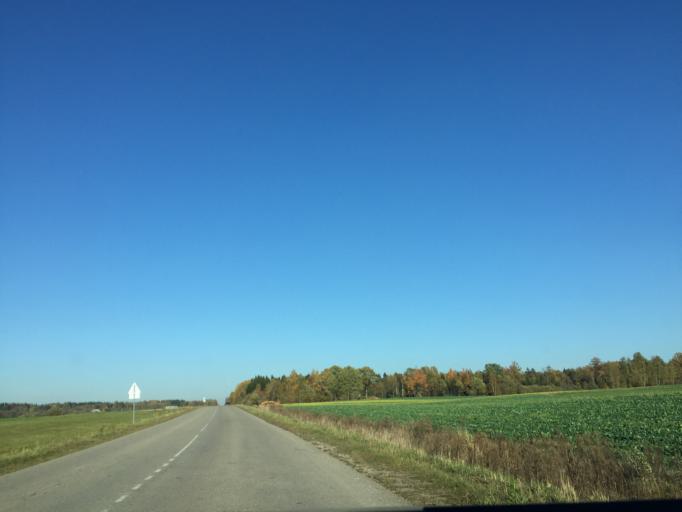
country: LT
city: Plateliai
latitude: 55.9998
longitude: 21.6909
